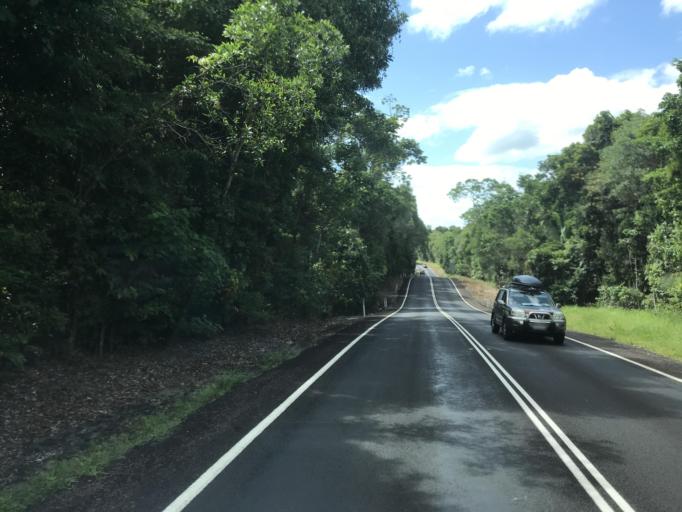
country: AU
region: Queensland
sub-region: Cassowary Coast
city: Innisfail
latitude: -17.8630
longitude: 146.0656
